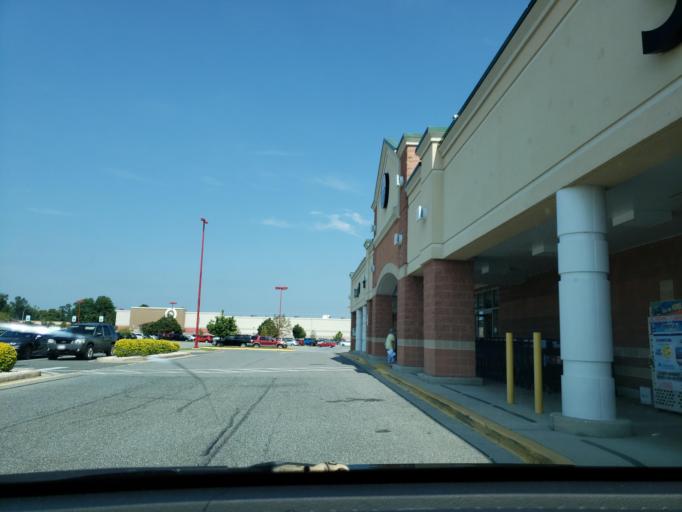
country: US
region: Delaware
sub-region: Kent County
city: Dover
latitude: 39.1587
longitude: -75.5090
